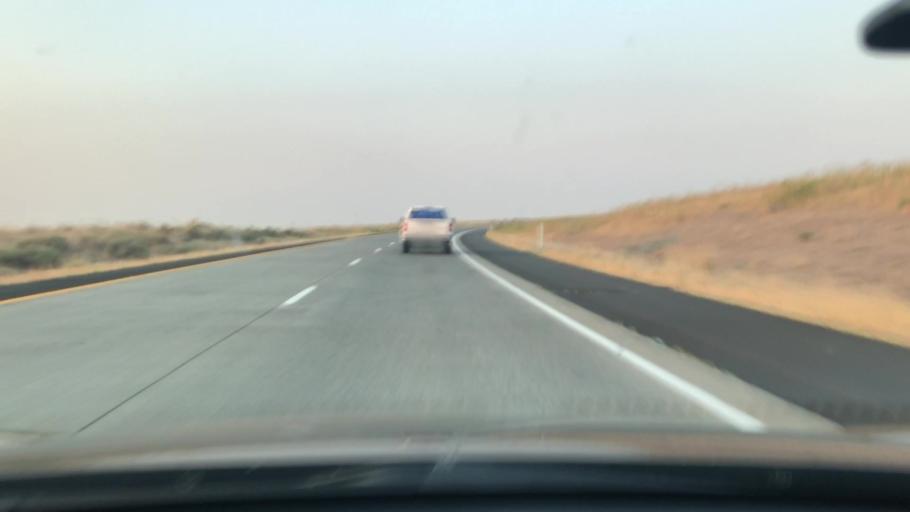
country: US
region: Washington
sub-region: Franklin County
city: Connell
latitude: 46.5918
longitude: -118.9584
